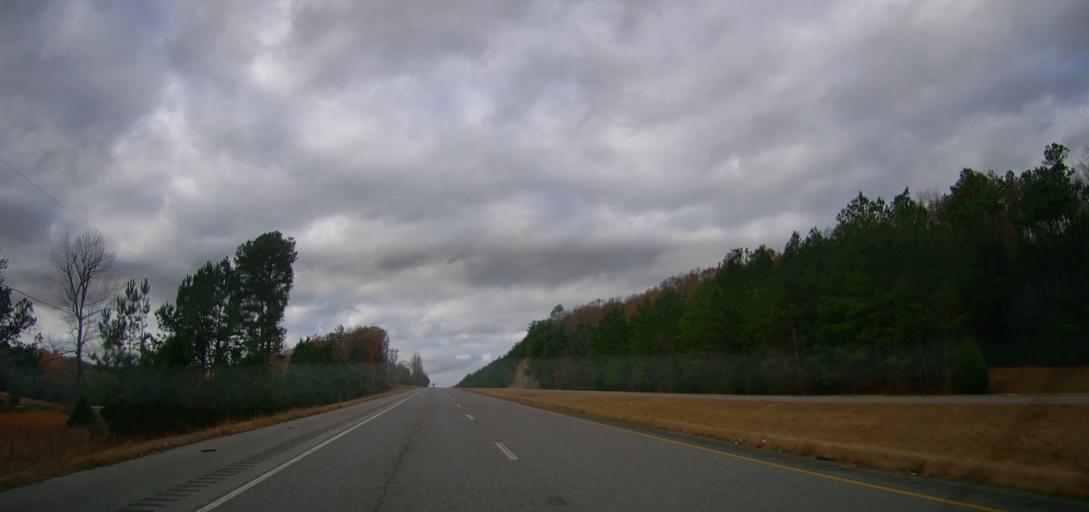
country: US
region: Alabama
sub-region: Lawrence County
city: Town Creek
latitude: 34.6145
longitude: -87.4612
